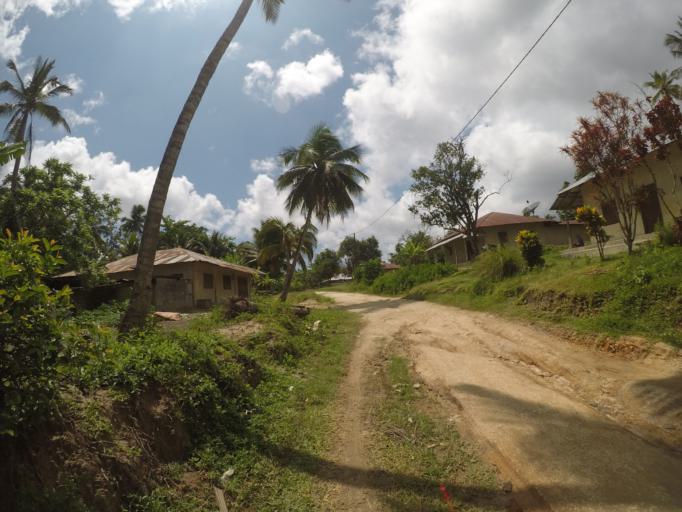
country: TZ
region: Pemba South
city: Mtambile
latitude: -5.3914
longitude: 39.7382
